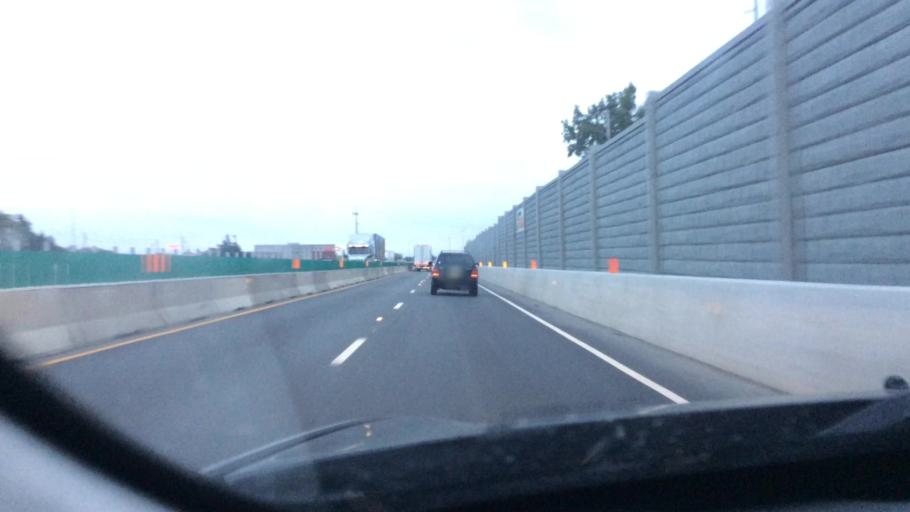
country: US
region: Ohio
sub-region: Hancock County
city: Findlay
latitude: 41.0665
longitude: -83.6649
